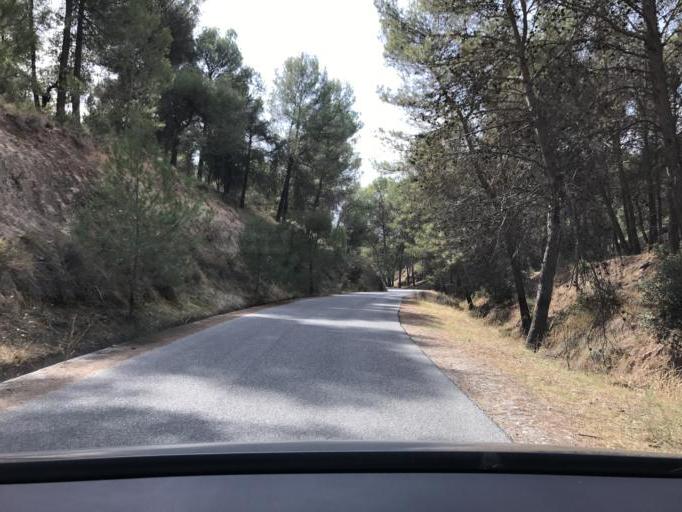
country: ES
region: Andalusia
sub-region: Provincia de Granada
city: Granada
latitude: 37.1925
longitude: -3.5709
